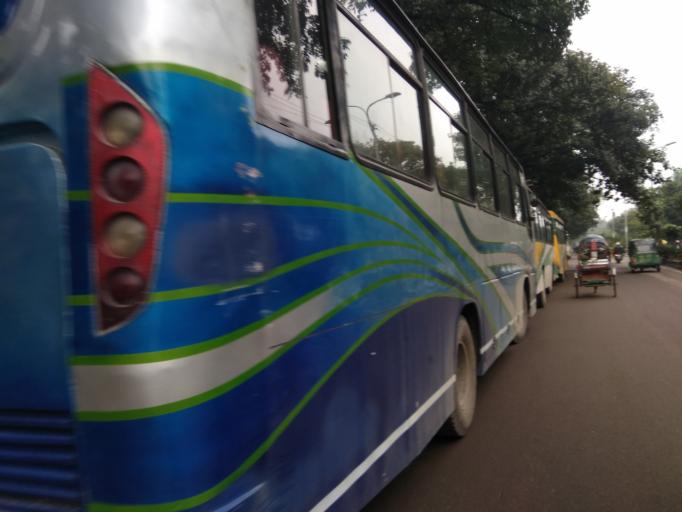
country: BD
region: Dhaka
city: Azimpur
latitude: 23.7308
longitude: 90.3976
